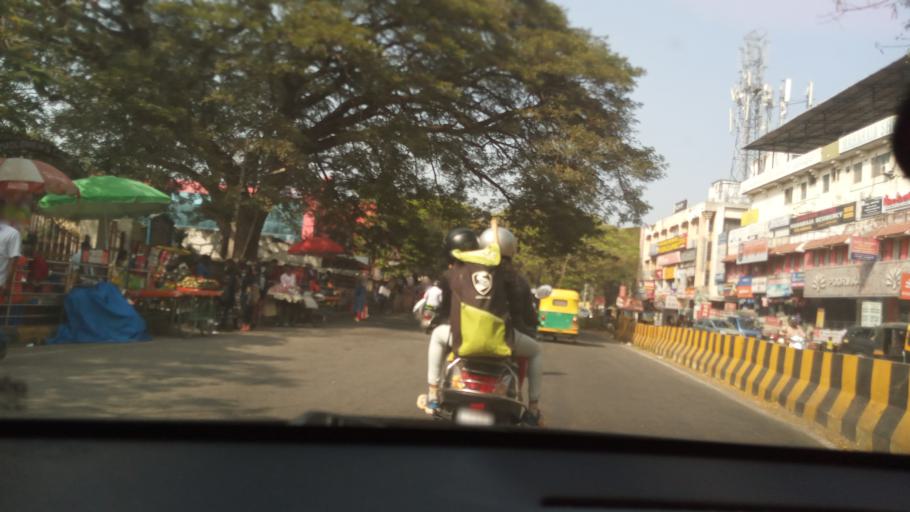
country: IN
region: Karnataka
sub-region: Mysore
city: Mysore
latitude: 12.3110
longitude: 76.6587
